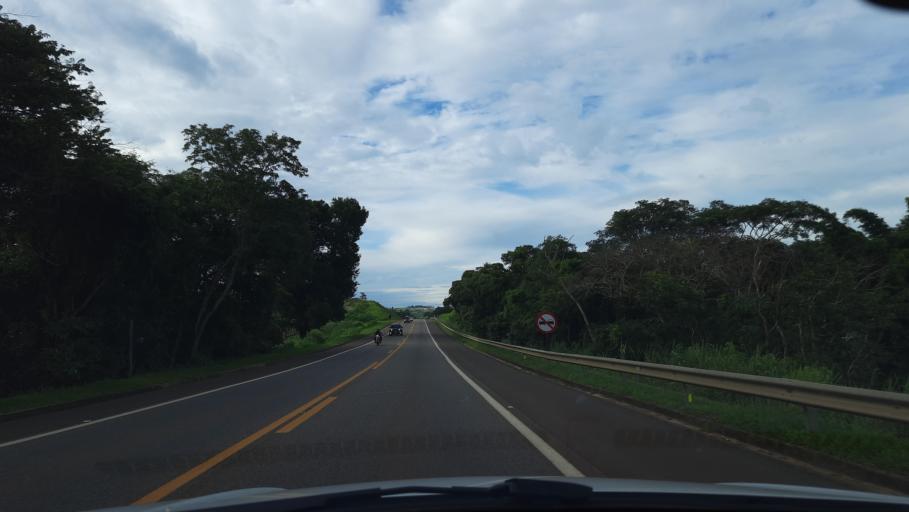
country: BR
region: Sao Paulo
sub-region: Vargem Grande Do Sul
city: Vargem Grande do Sul
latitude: -21.8907
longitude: -46.8667
